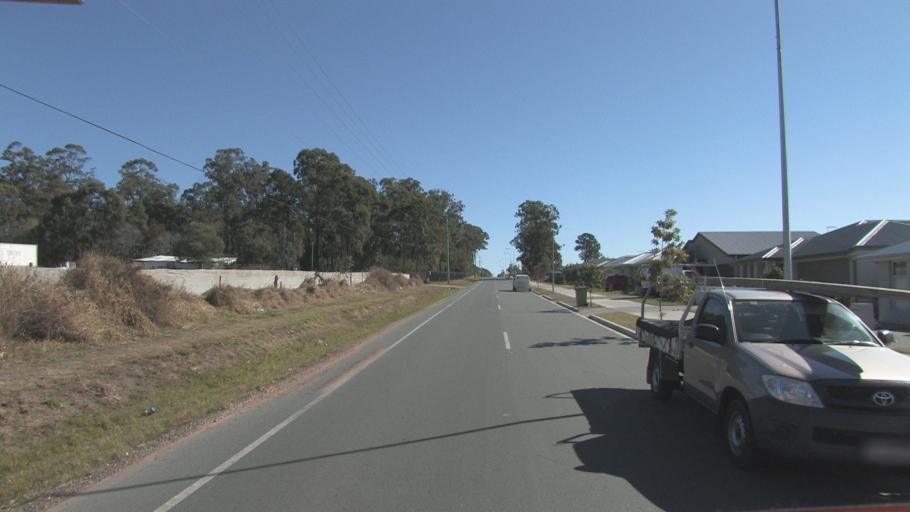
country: AU
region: Queensland
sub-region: Logan
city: Logan Reserve
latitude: -27.7172
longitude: 153.0860
